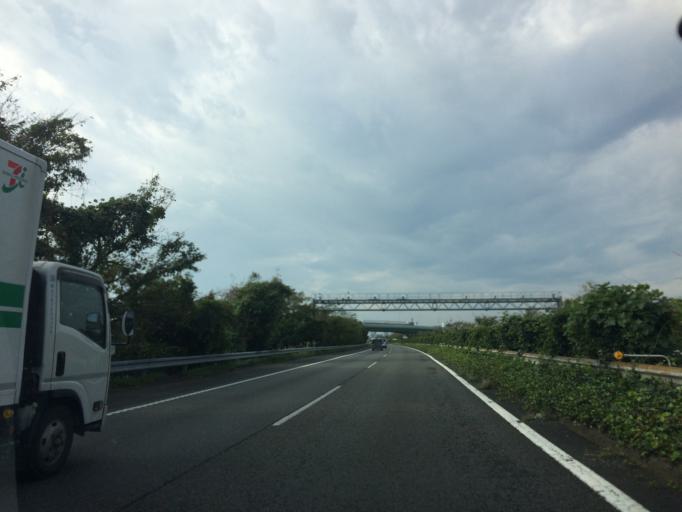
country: JP
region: Shizuoka
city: Shizuoka-shi
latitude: 35.0170
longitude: 138.4387
